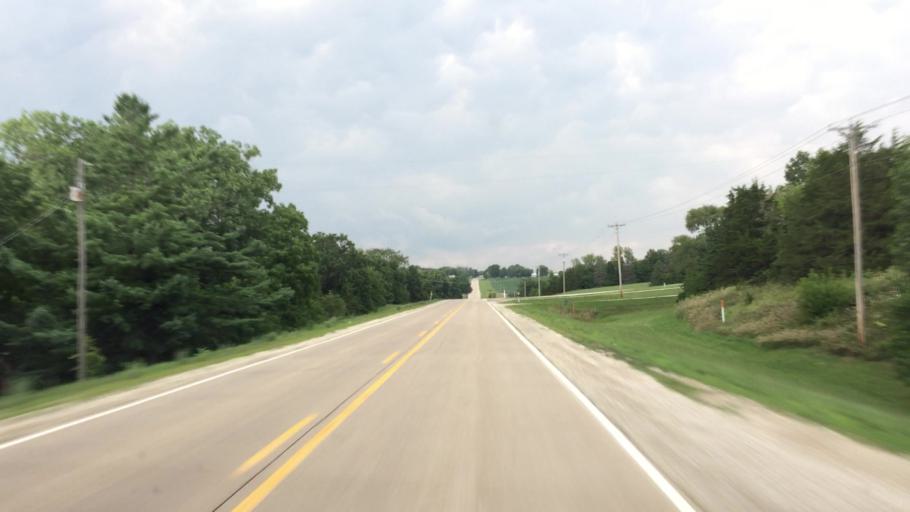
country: US
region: Iowa
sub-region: Lee County
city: Fort Madison
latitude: 40.7186
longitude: -91.3299
